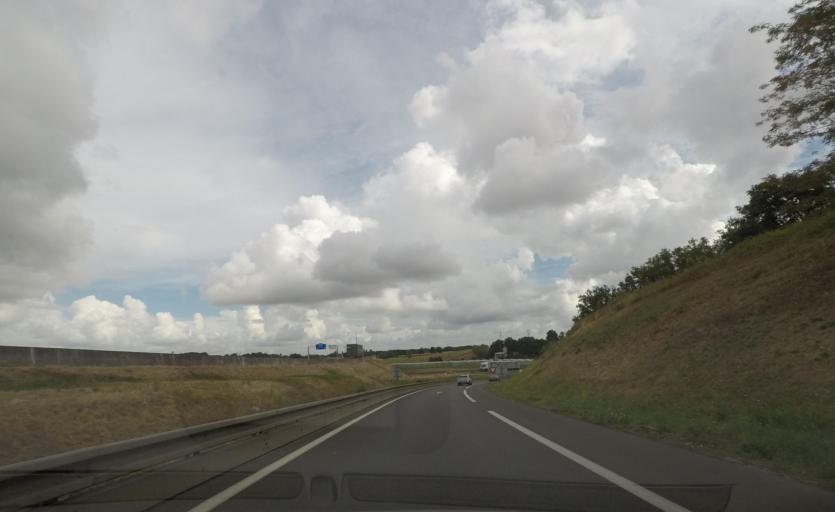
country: FR
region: Pays de la Loire
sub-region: Departement de Maine-et-Loire
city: Ecouflant
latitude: 47.5011
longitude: -0.5008
